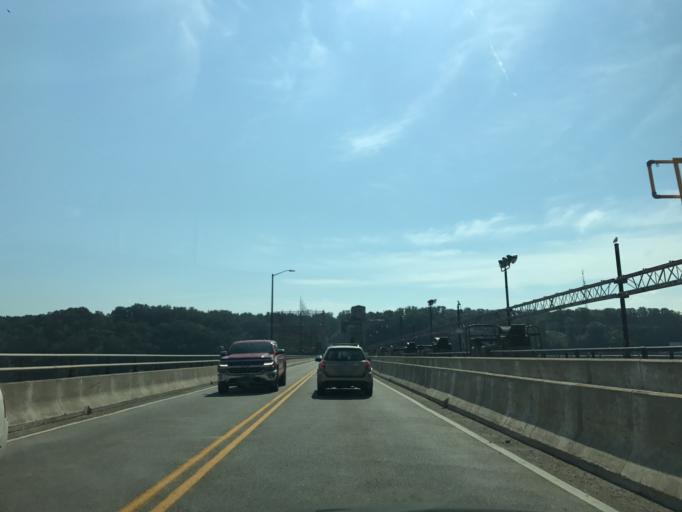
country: US
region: Maryland
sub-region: Cecil County
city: Rising Sun
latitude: 39.6611
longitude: -76.1732
